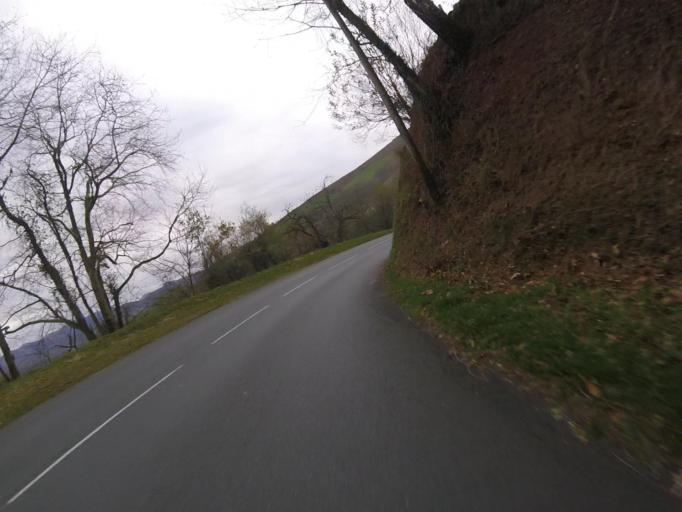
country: FR
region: Aquitaine
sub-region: Departement des Pyrenees-Atlantiques
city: Sare
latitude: 43.3207
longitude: -1.5979
